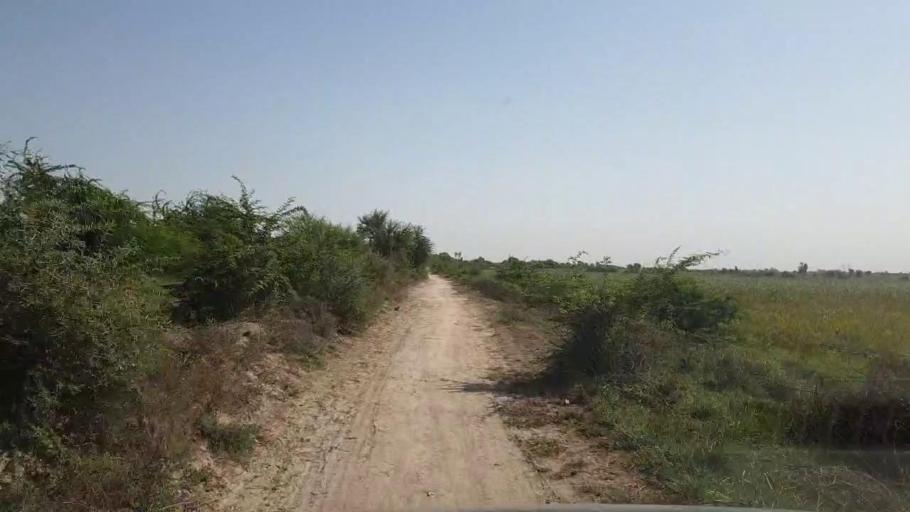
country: PK
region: Sindh
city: Kadhan
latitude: 24.6061
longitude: 69.0020
